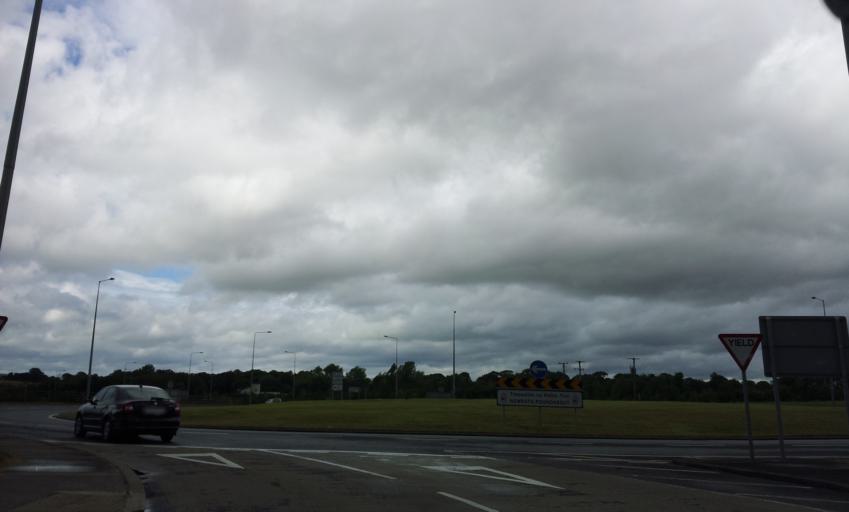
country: IE
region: Munster
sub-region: Waterford
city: Waterford
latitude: 52.2766
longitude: -7.1323
